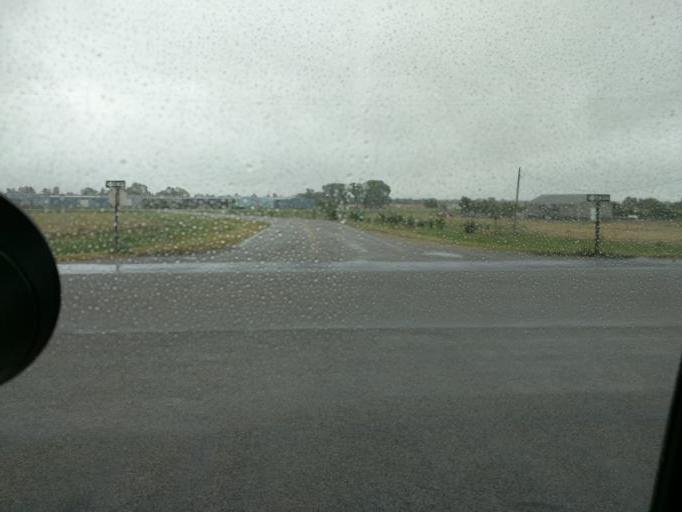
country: US
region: Kansas
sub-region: Reno County
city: South Hutchinson
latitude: 37.9441
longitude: -97.8842
